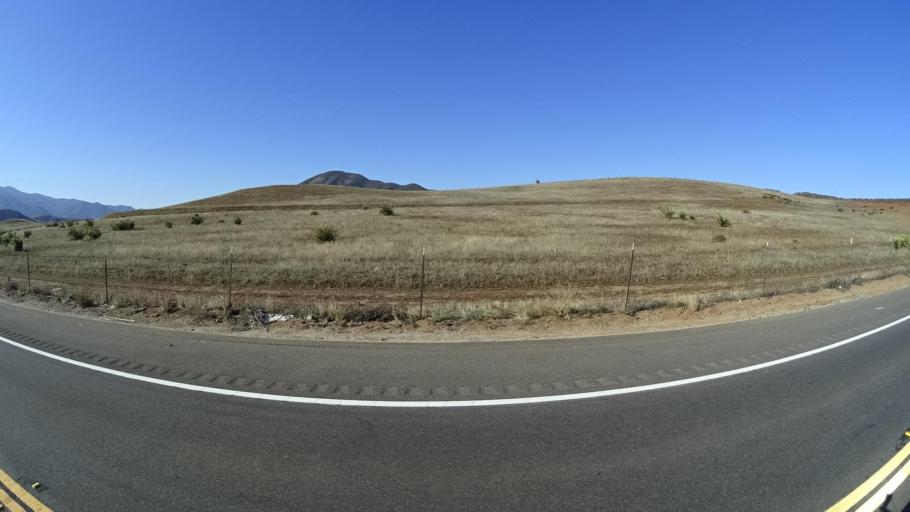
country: US
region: California
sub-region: San Diego County
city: Jamul
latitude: 32.7006
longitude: -116.8644
